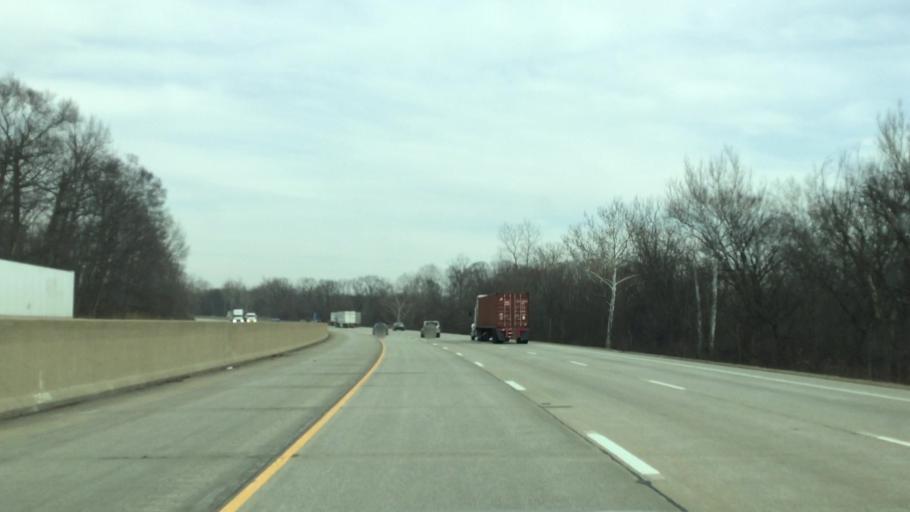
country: US
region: Indiana
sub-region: LaPorte County
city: Trail Creek
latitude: 41.6584
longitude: -86.8778
